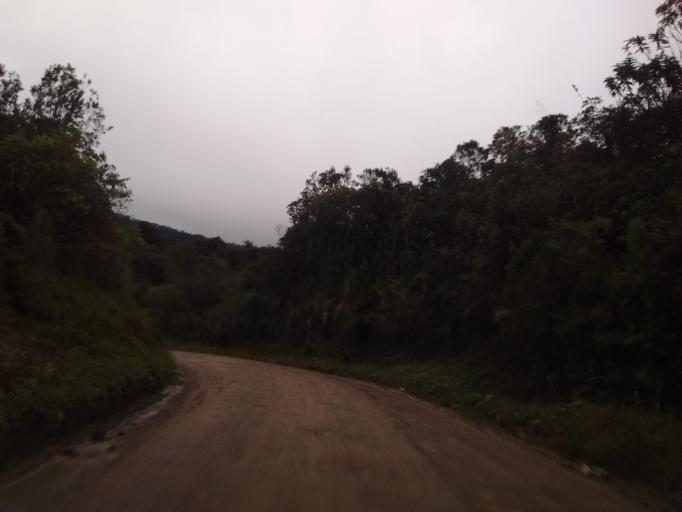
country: CO
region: Huila
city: Isnos
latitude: 2.1307
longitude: -76.3792
